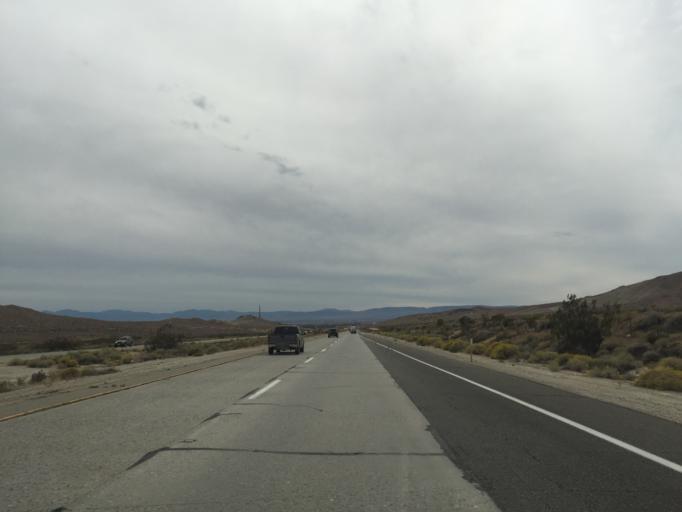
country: US
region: California
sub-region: Kern County
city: Rosamond
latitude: 34.9029
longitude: -118.1651
